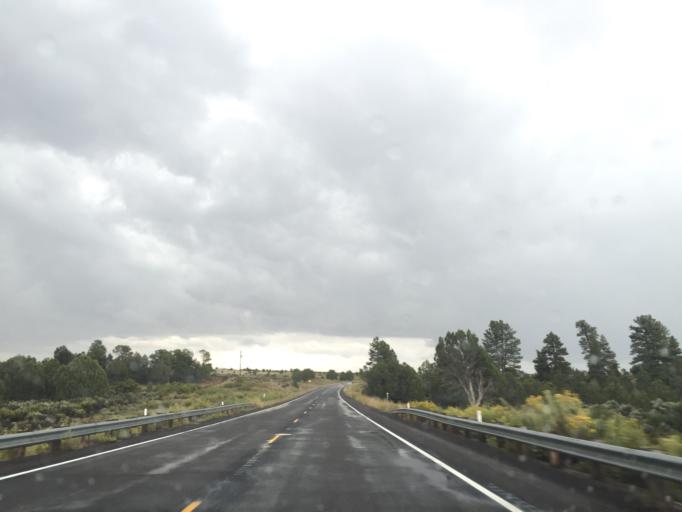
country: US
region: Utah
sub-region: Kane County
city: Kanab
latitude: 37.2325
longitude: -112.7349
